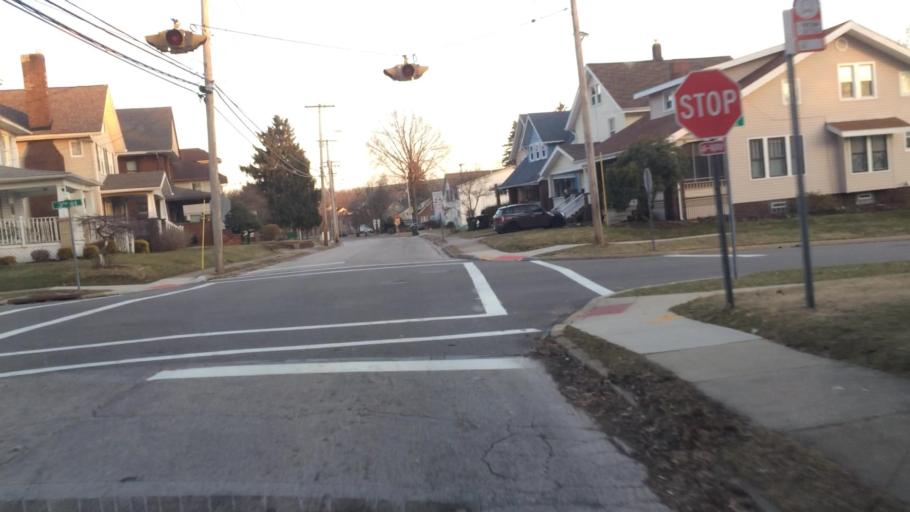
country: US
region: Ohio
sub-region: Summit County
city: Cuyahoga Falls
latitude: 41.1442
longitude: -81.4796
